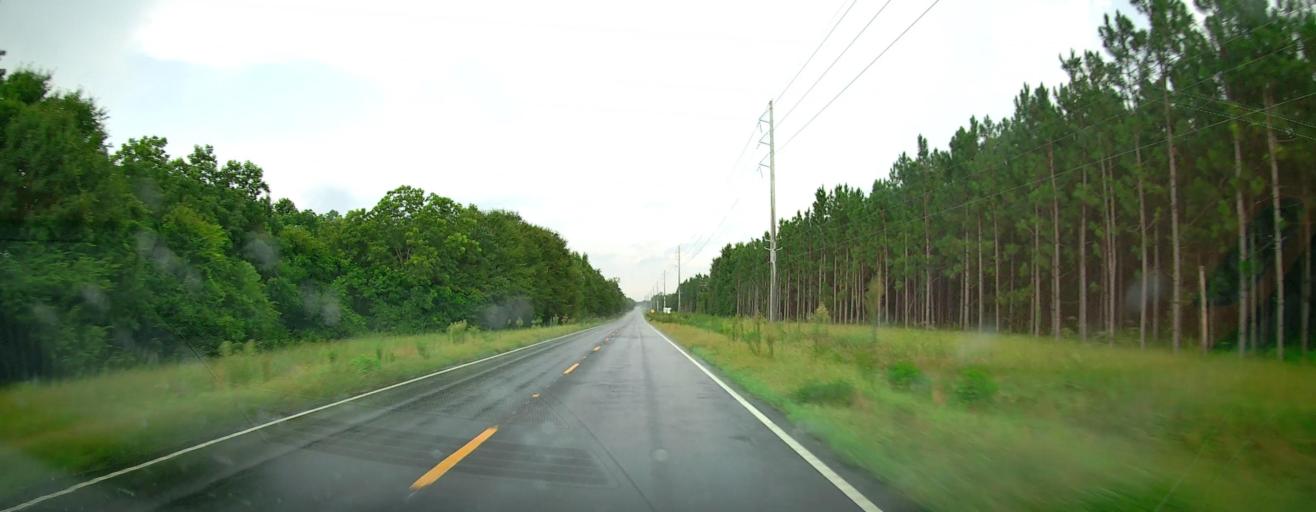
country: US
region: Georgia
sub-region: Dodge County
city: Chester
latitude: 32.5691
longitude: -83.1841
